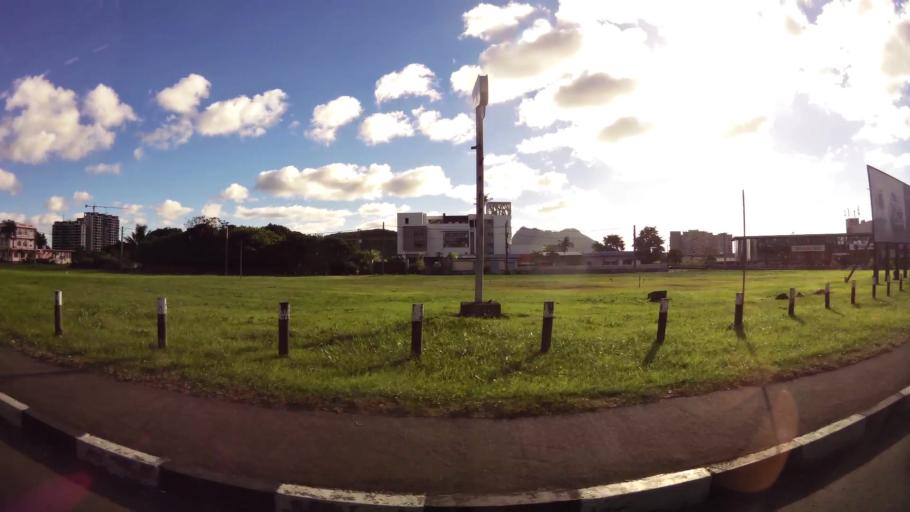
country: MU
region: Plaines Wilhems
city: Quatre Bornes
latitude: -20.2743
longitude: 57.4969
